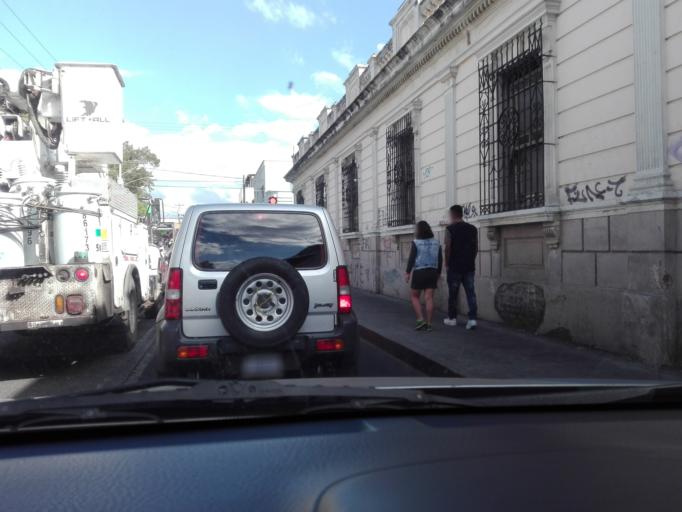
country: GT
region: Guatemala
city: Guatemala City
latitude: 14.6459
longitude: -90.5137
